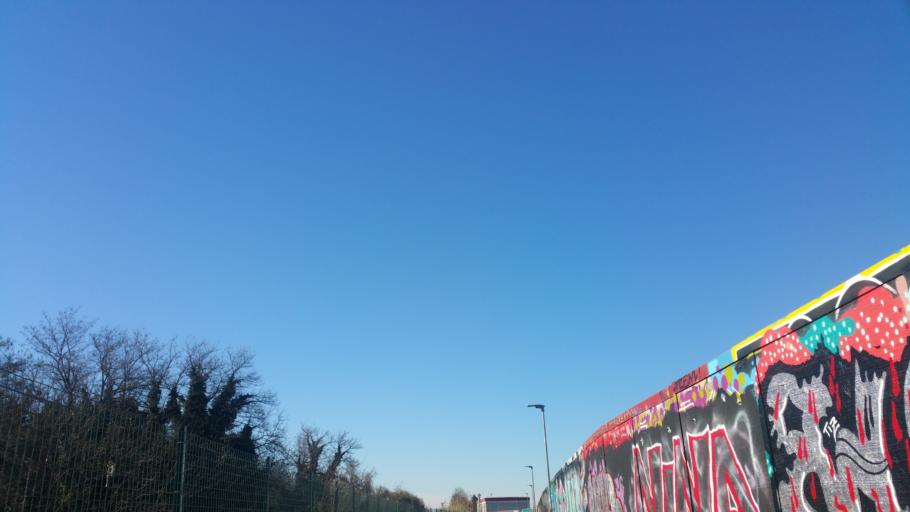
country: IT
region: Emilia-Romagna
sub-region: Provincia di Bologna
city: Bologna
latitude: 44.5032
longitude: 11.3217
